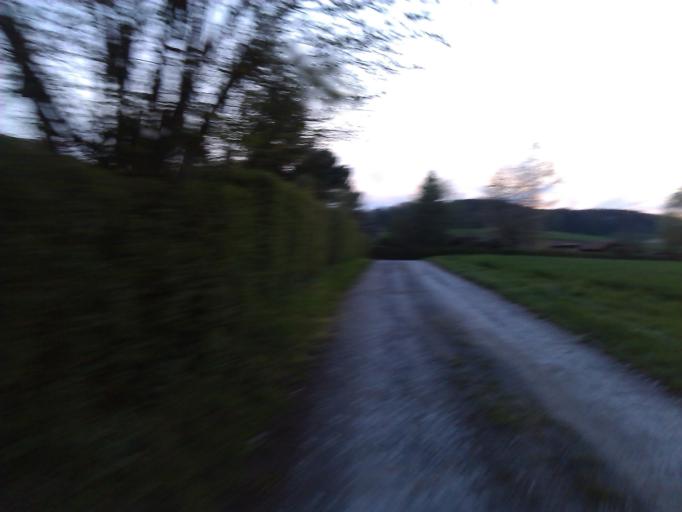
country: DE
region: Baden-Wuerttemberg
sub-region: Regierungsbezirk Stuttgart
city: Untereisesheim
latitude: 49.2120
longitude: 9.1845
